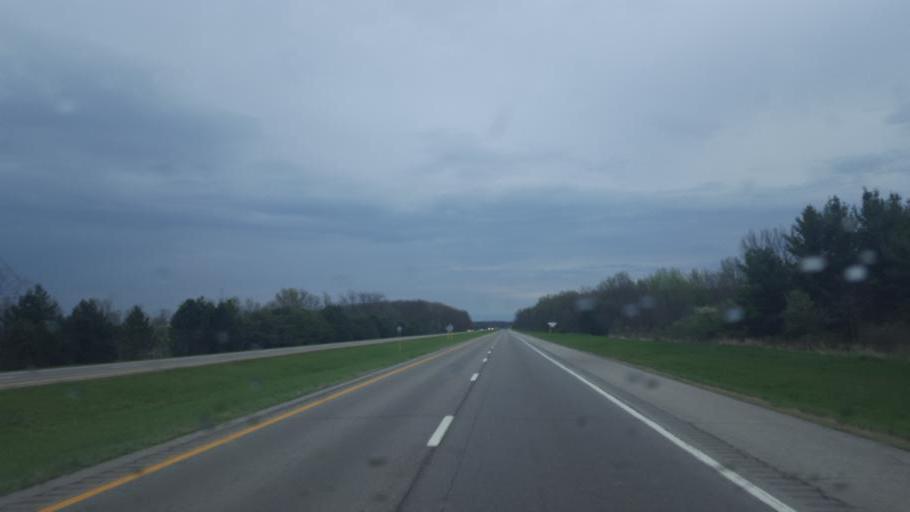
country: US
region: Ohio
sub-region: Wyandot County
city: Carey
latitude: 40.9321
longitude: -83.3806
